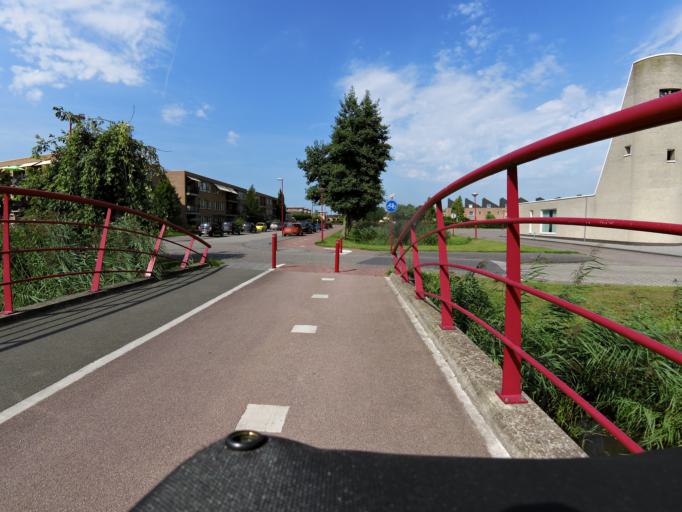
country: NL
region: South Holland
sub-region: Gemeente Oud-Beijerland
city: Oud-Beijerland
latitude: 51.8159
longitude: 4.4312
